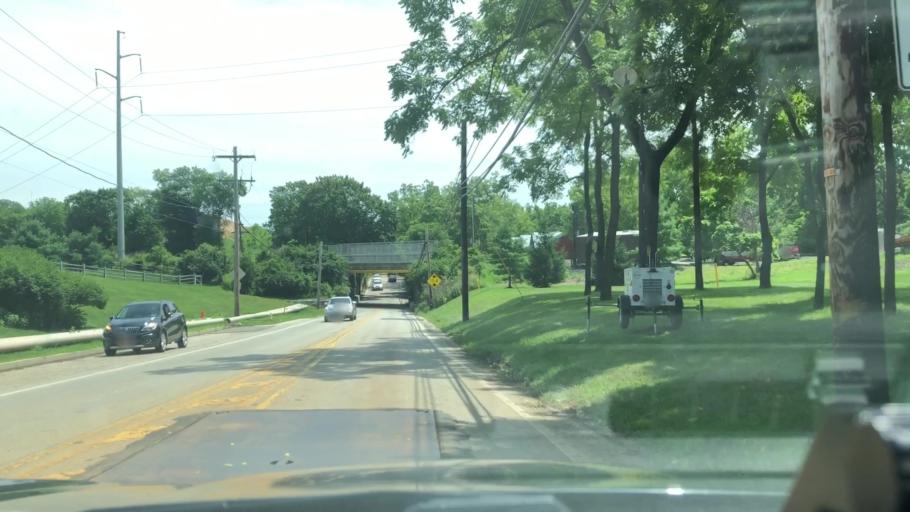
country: US
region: Pennsylvania
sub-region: Montgomery County
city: Plymouth Meeting
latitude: 40.1082
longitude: -75.2692
